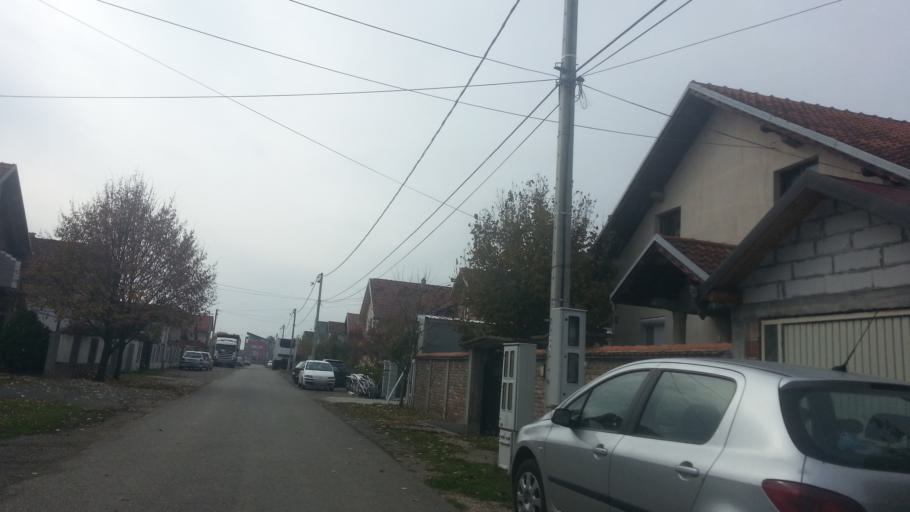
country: RS
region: Autonomna Pokrajina Vojvodina
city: Nova Pazova
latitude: 44.9557
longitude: 20.2102
